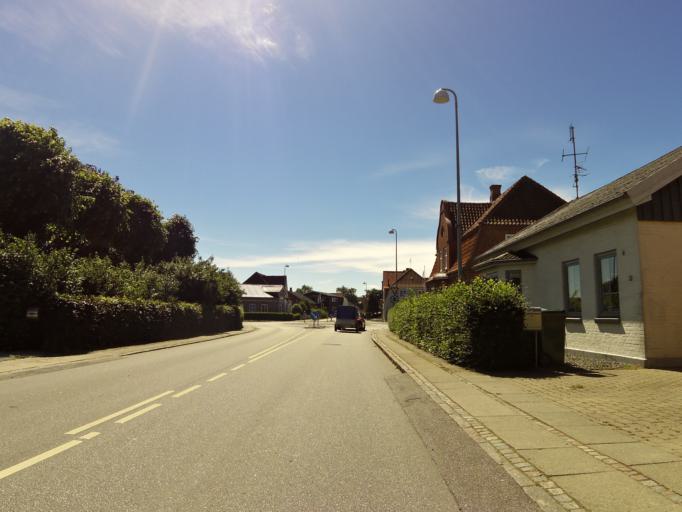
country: DK
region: South Denmark
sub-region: Aabenraa Kommune
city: Rodekro
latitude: 55.0245
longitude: 9.3117
